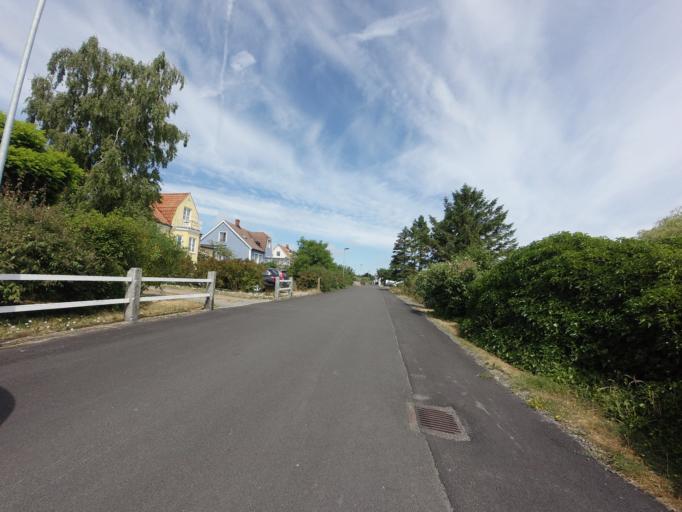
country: SE
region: Skane
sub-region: Simrishamns Kommun
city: Simrishamn
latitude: 55.5454
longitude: 14.3568
